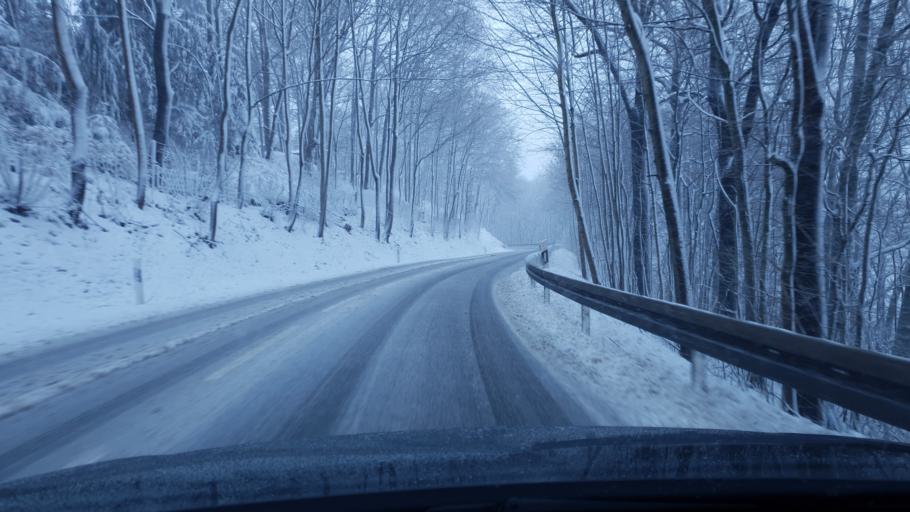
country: DE
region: Saxony
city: Wittgensdorf
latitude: 50.9005
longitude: 12.9001
